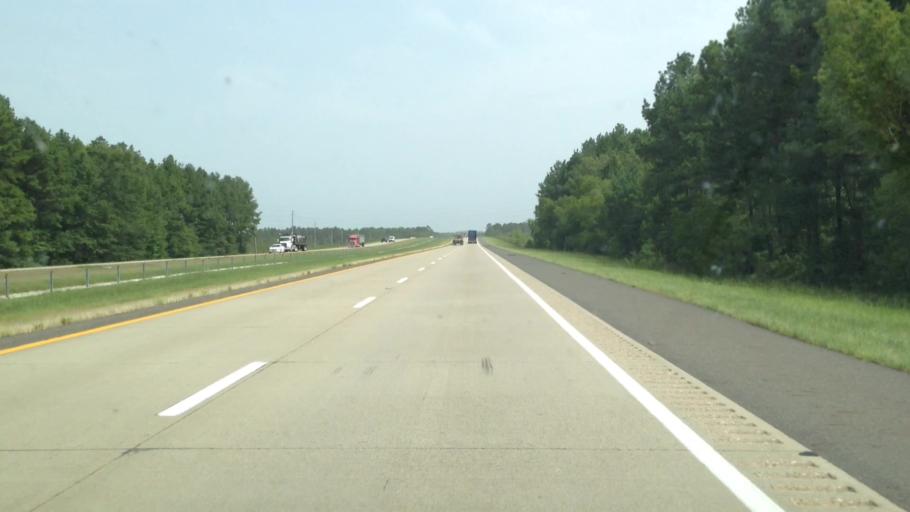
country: US
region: Texas
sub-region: Bowie County
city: Texarkana
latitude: 33.2189
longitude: -93.8734
